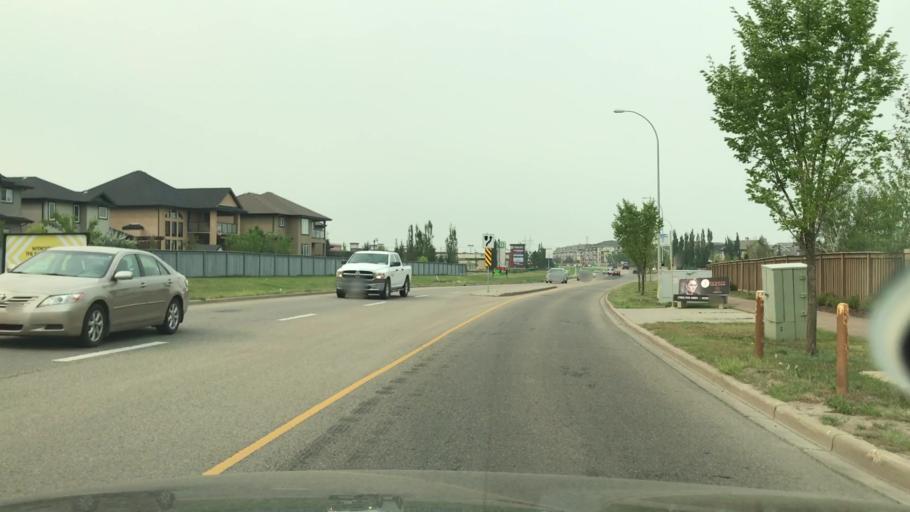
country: CA
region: Alberta
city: Edmonton
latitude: 53.4373
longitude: -113.5684
